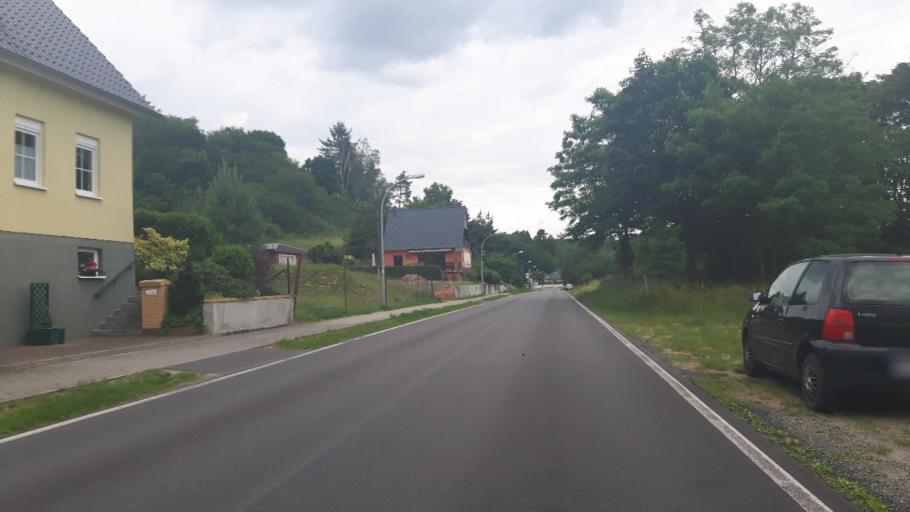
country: DE
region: Brandenburg
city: Niederfinow
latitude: 52.8410
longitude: 13.9374
